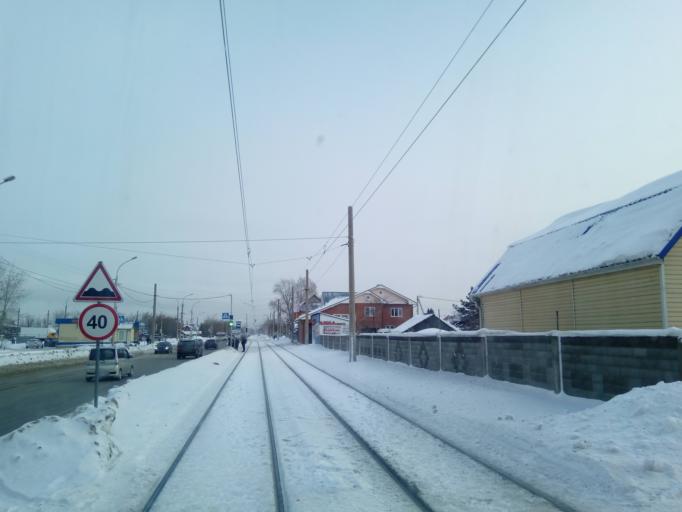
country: RU
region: Novosibirsk
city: Tolmachevo
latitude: 54.9801
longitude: 82.8327
